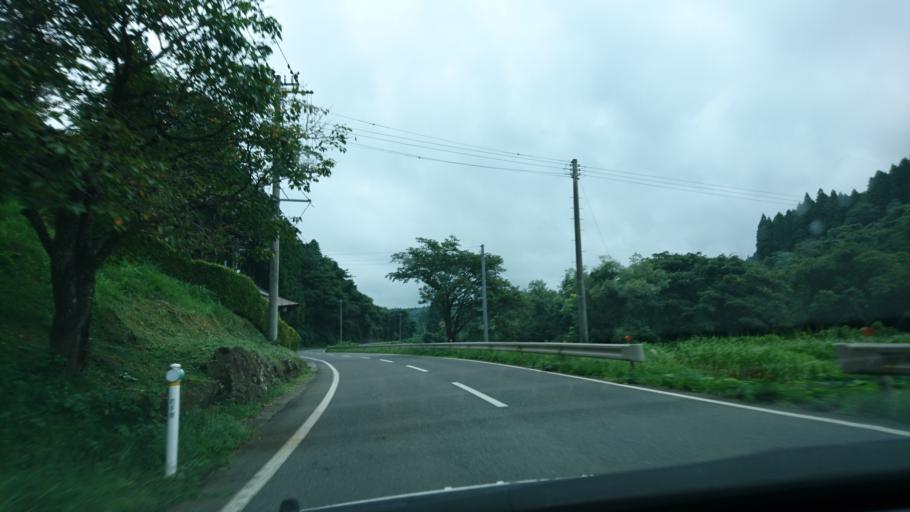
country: JP
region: Iwate
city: Ichinoseki
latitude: 38.9106
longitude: 141.0567
